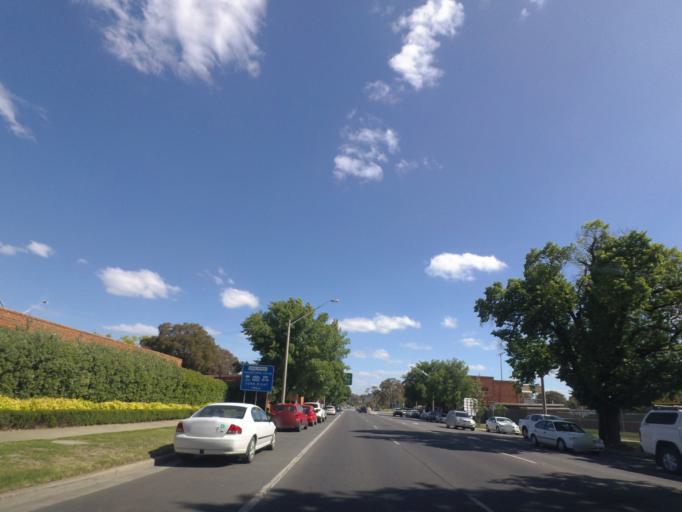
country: AU
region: New South Wales
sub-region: Albury Municipality
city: South Albury
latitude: -36.0824
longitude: 146.9102
